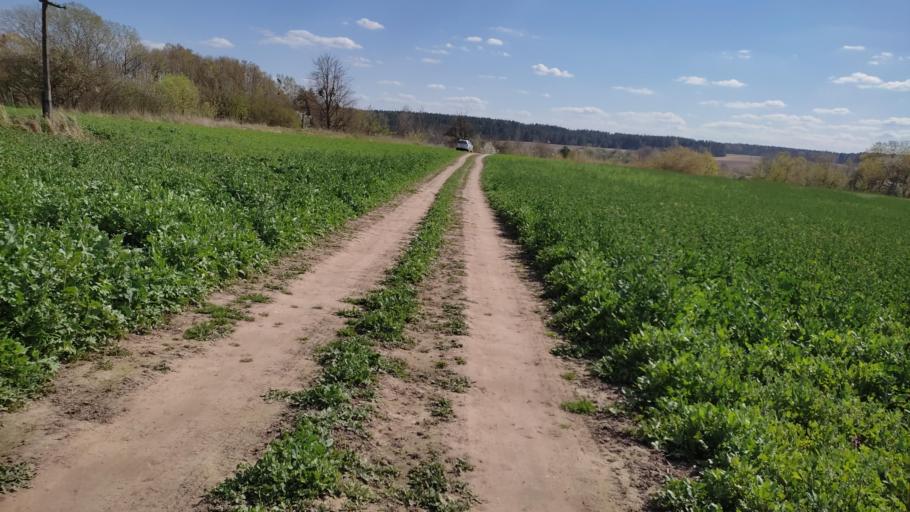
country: BY
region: Grodnenskaya
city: Hrodna
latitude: 53.6552
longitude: 23.9057
